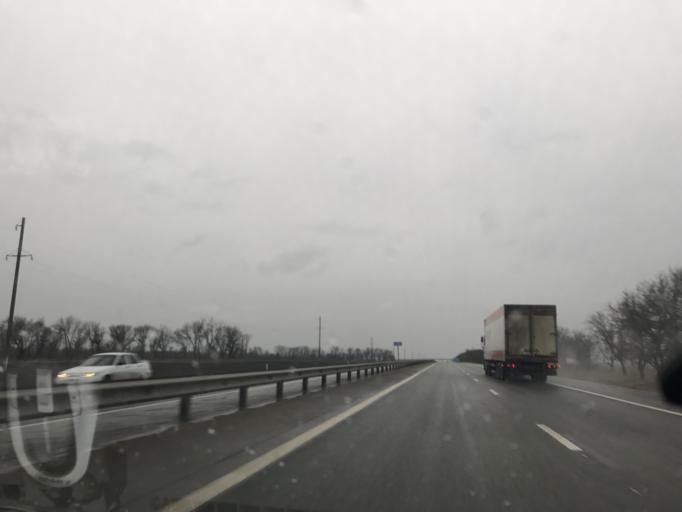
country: RU
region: Krasnodarskiy
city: Kislyakovskaya
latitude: 46.3954
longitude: 39.7334
